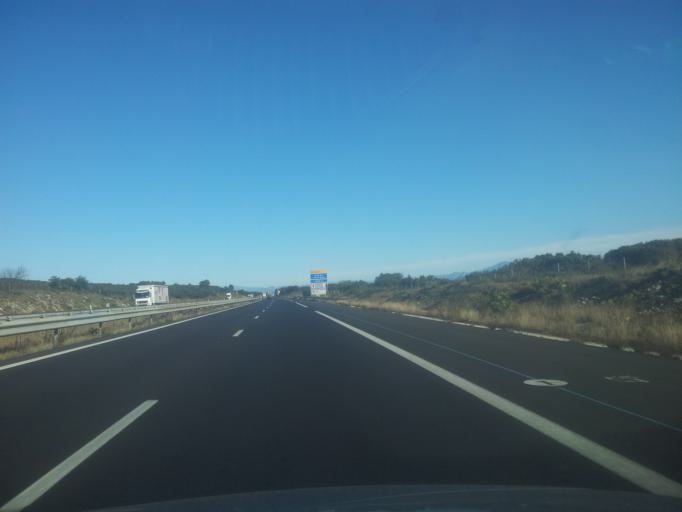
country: FR
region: Languedoc-Roussillon
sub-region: Departement du Gard
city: Rochefort-du-Gard
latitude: 43.9910
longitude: 4.6863
